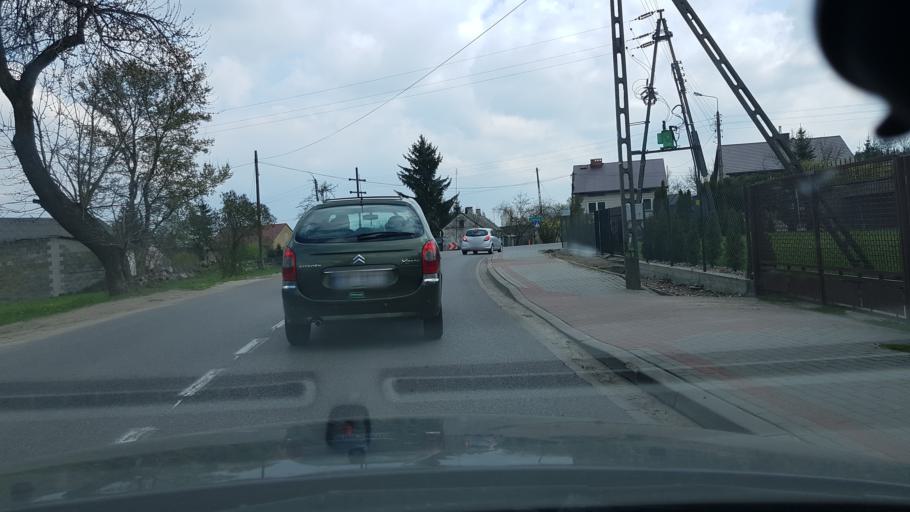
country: PL
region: Masovian Voivodeship
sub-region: Powiat minski
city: Kaluszyn
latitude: 52.1959
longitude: 21.8099
